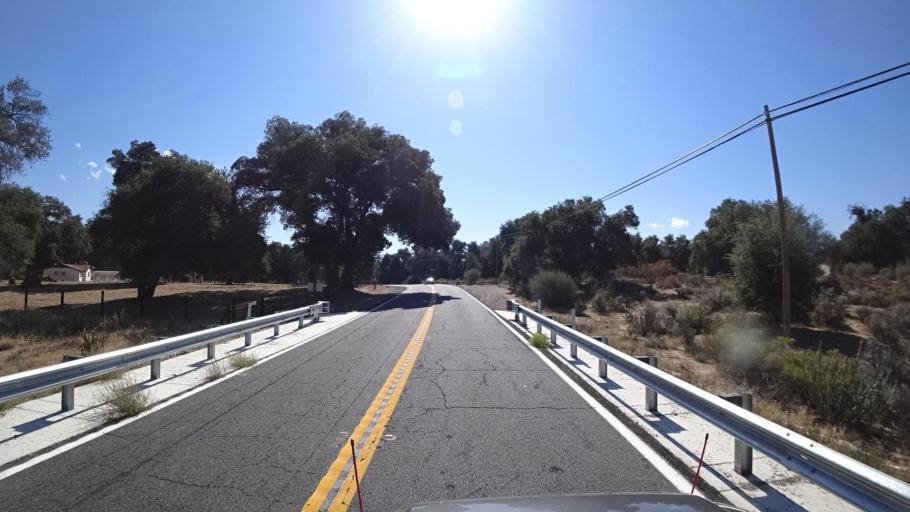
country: US
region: California
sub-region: Riverside County
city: Aguanga
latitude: 33.3313
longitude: -116.7098
